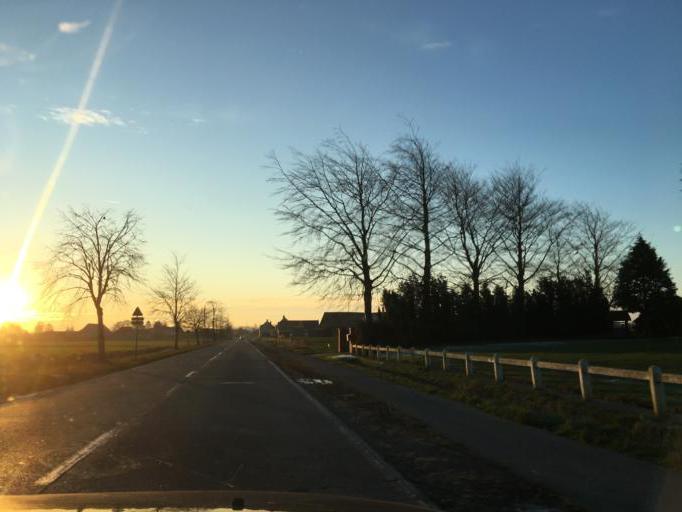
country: BE
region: Flanders
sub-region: Provincie Oost-Vlaanderen
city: Zomergem
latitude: 51.1490
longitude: 3.5295
